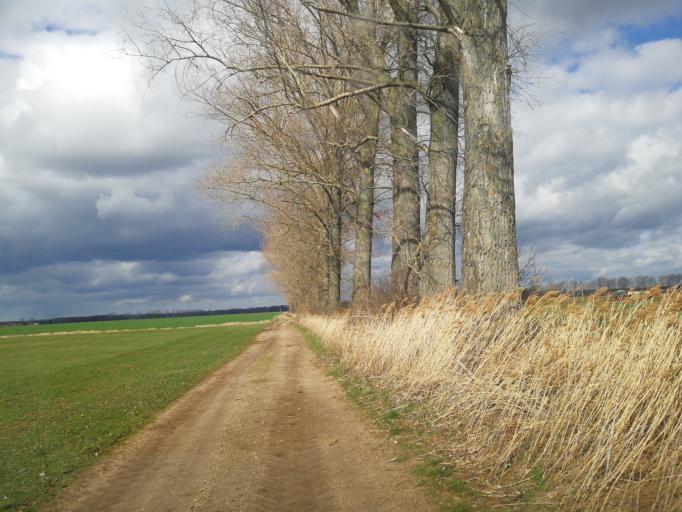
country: DE
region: Brandenburg
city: Schonewalde
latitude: 51.6780
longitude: 13.5581
